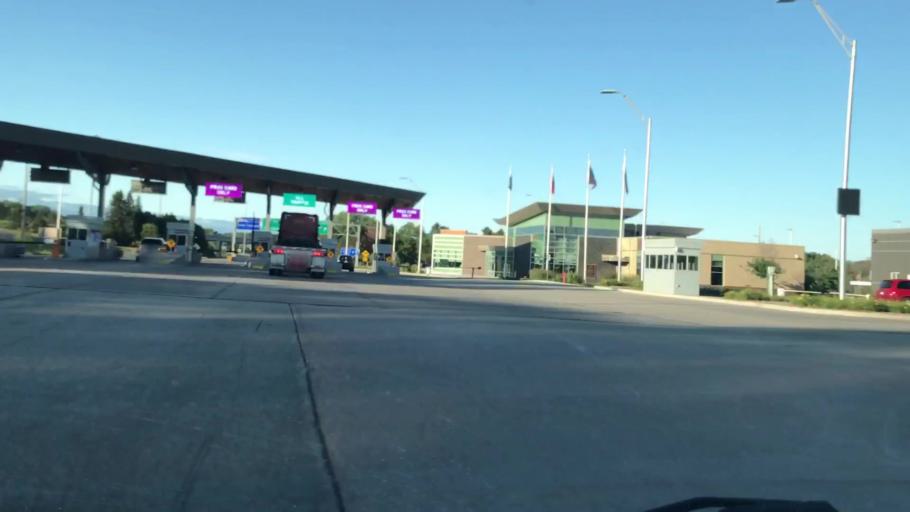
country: US
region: Michigan
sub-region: Chippewa County
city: Sault Ste. Marie
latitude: 46.4942
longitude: -84.3682
